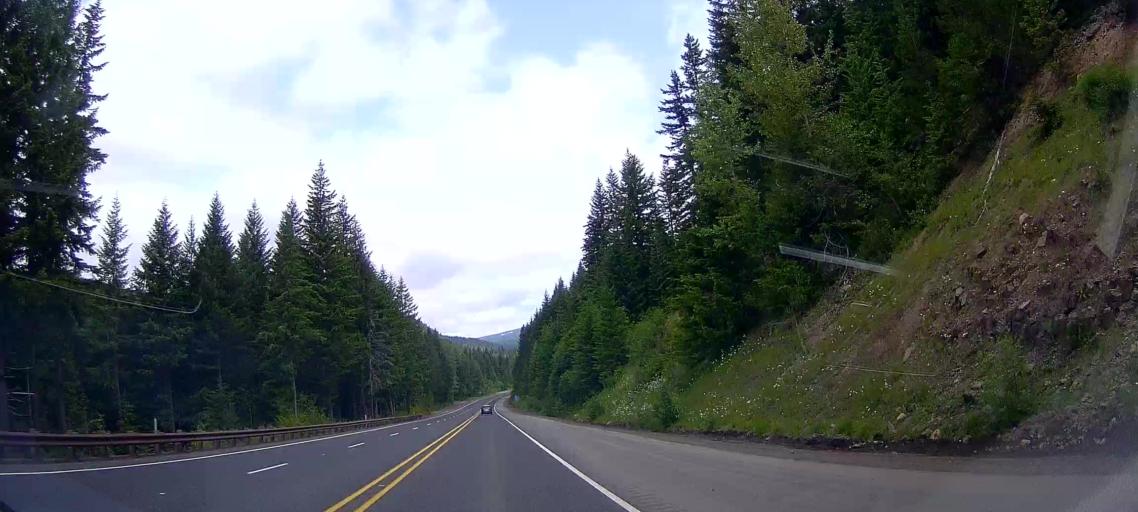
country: US
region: Oregon
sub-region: Clackamas County
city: Mount Hood Village
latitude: 45.2456
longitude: -121.7082
